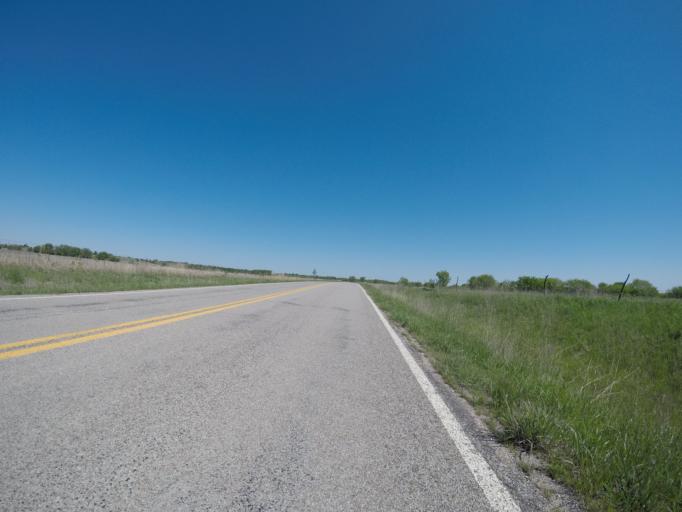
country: US
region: Kansas
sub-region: Osage County
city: Overbrook
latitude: 38.8704
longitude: -95.5565
